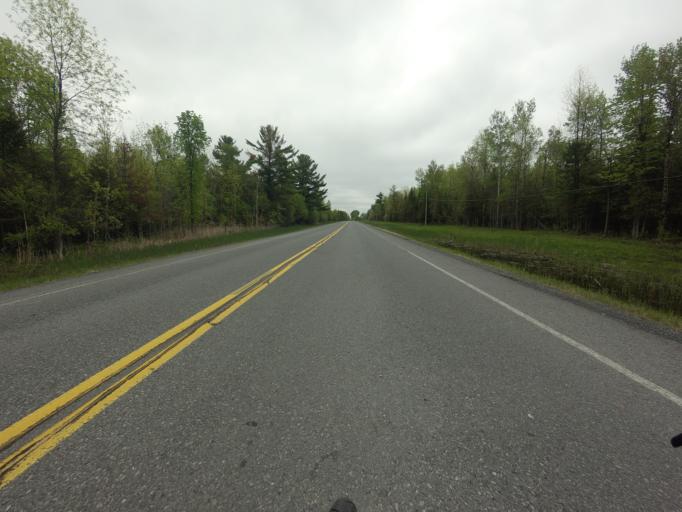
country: US
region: New York
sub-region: St. Lawrence County
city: Norfolk
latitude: 44.9349
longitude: -75.1447
